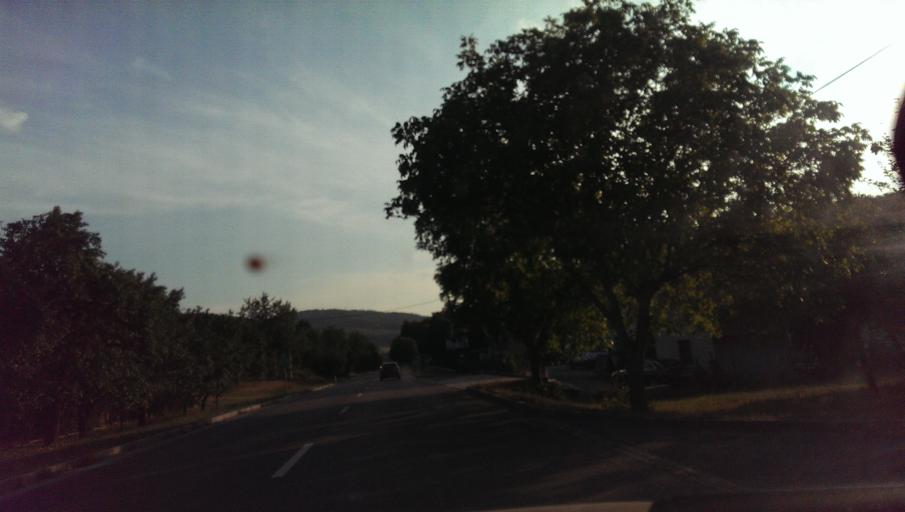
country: CZ
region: Zlin
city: Pozlovice
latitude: 49.1349
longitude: 17.8094
